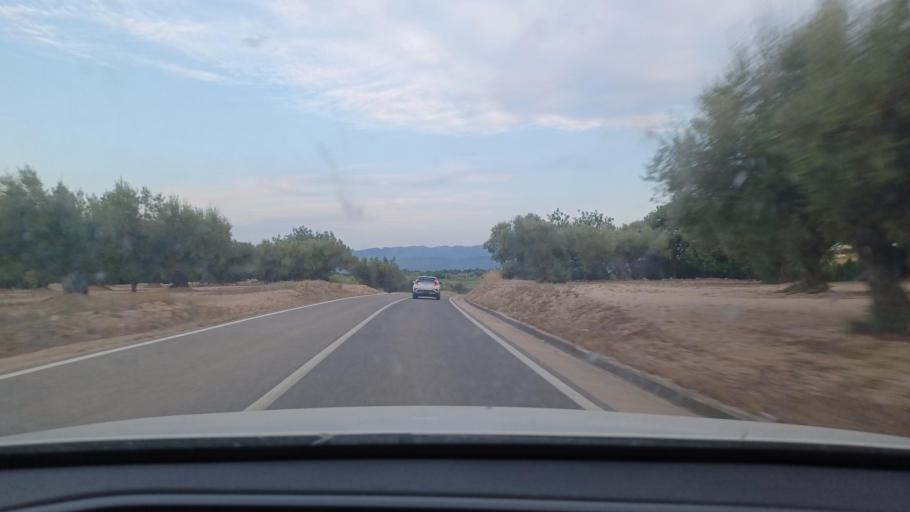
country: ES
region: Catalonia
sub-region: Provincia de Tarragona
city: Mas de Barberans
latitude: 40.7180
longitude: 0.4005
